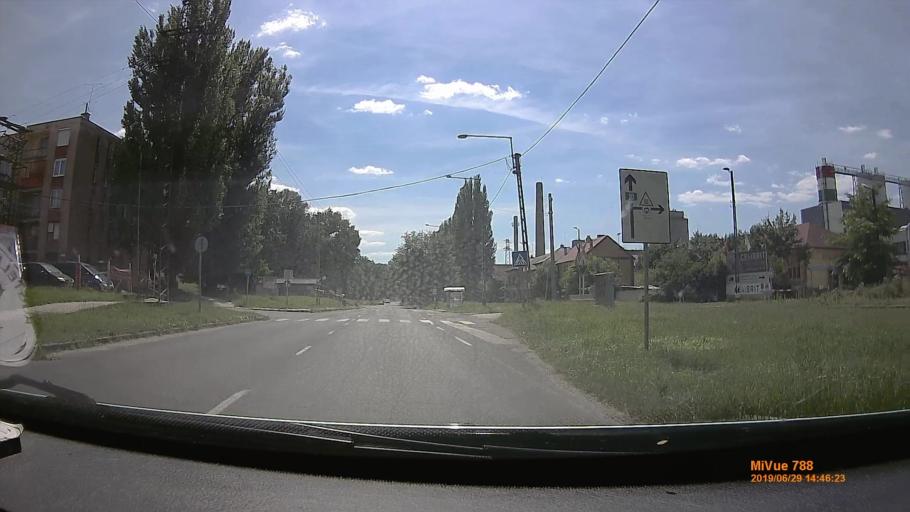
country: HU
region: Komarom-Esztergom
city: Nyergesujfalu
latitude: 47.7559
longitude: 18.5313
